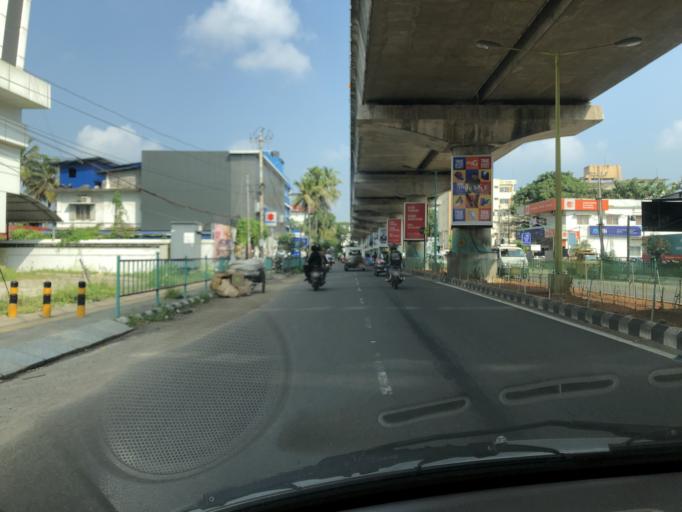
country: IN
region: Kerala
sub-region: Ernakulam
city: Elur
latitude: 10.0113
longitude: 76.3030
